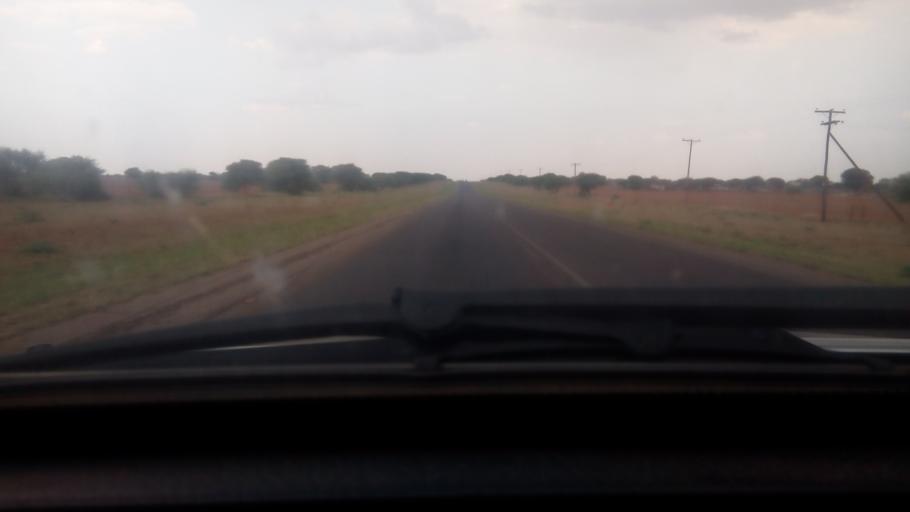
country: BW
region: Kweneng
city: Metsemotlhaba
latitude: -24.4702
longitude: 25.6895
